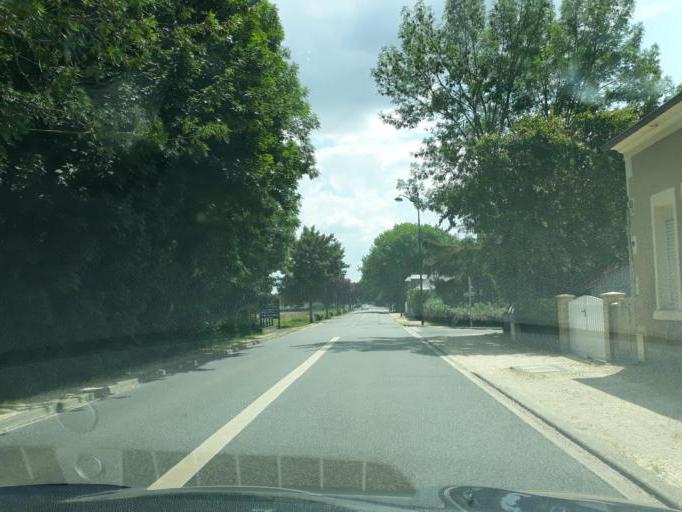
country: FR
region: Centre
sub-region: Departement du Cher
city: Avord
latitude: 47.0438
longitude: 2.5641
